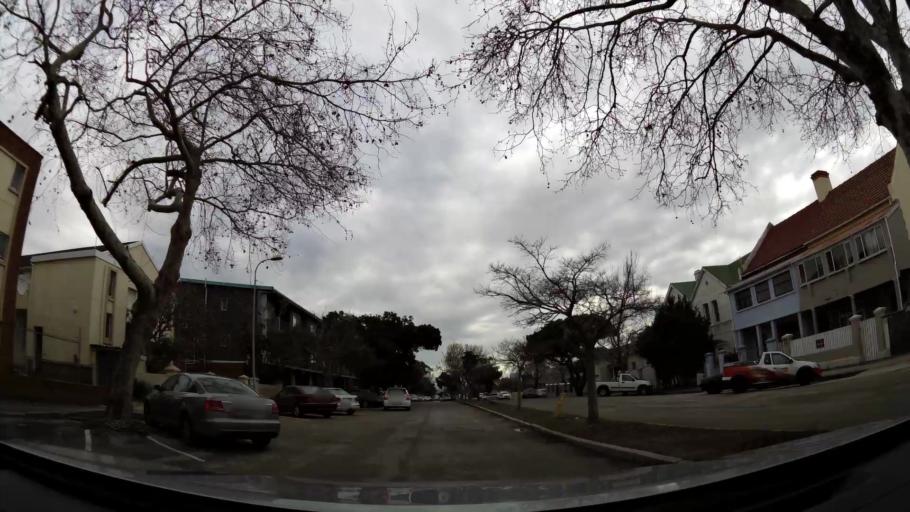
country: ZA
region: Eastern Cape
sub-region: Nelson Mandela Bay Metropolitan Municipality
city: Port Elizabeth
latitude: -33.9592
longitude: 25.6094
